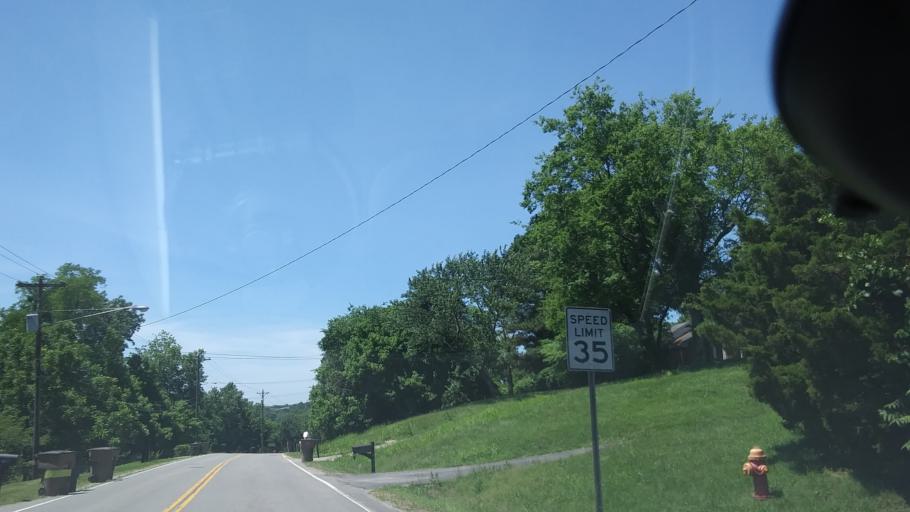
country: US
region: Tennessee
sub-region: Davidson County
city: Oak Hill
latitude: 36.0951
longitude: -86.6746
